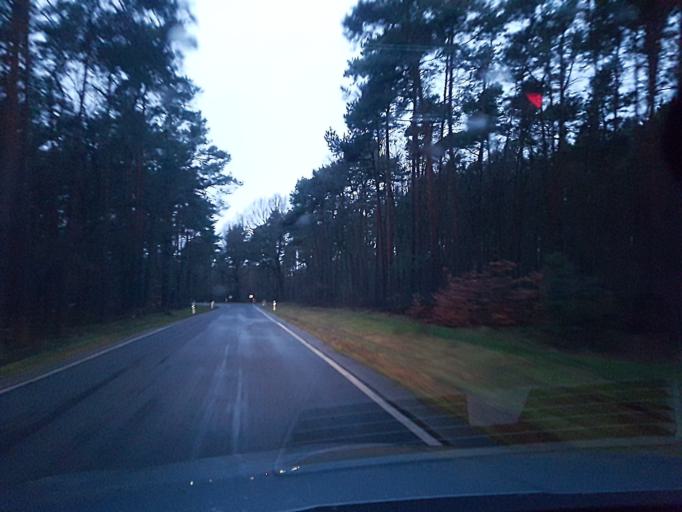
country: DE
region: Brandenburg
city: Bad Liebenwerda
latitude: 51.5465
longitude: 13.4307
